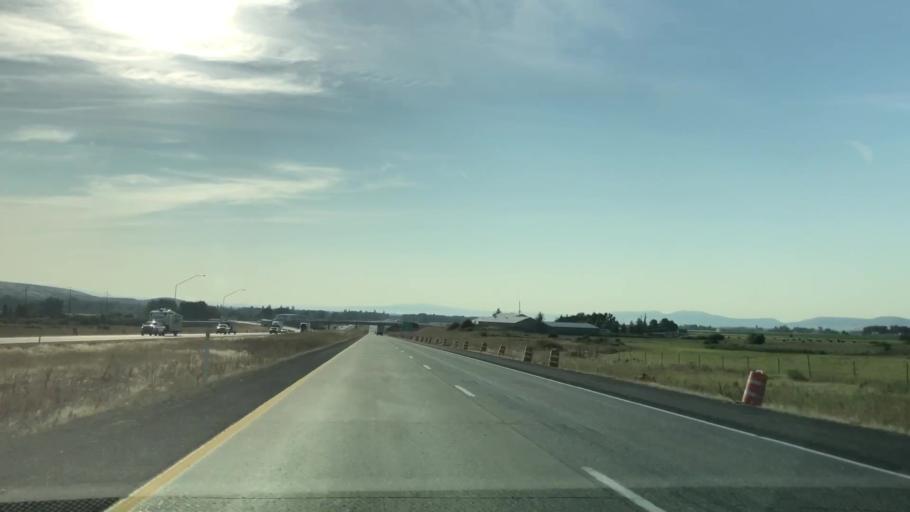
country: US
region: Washington
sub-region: Kittitas County
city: Ellensburg
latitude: 47.0574
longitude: -120.6760
